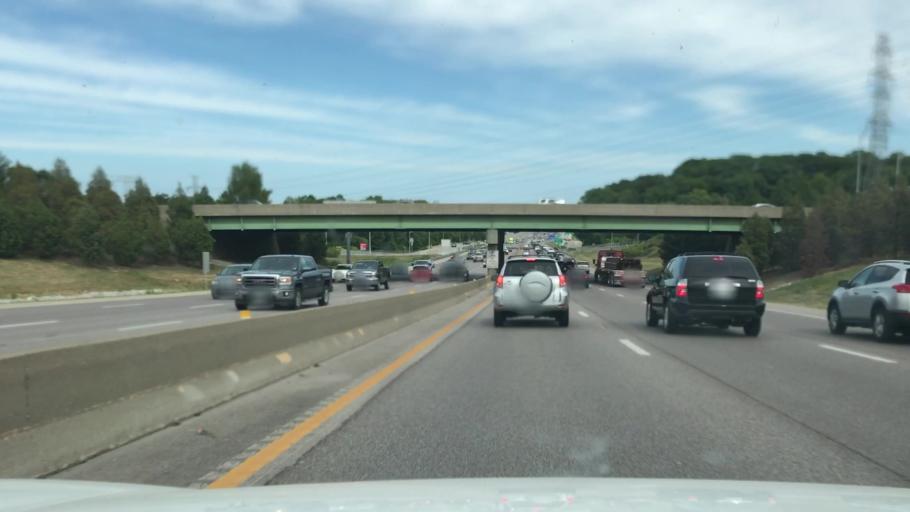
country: US
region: Missouri
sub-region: Saint Louis County
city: Chesterfield
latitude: 38.6469
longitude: -90.5314
